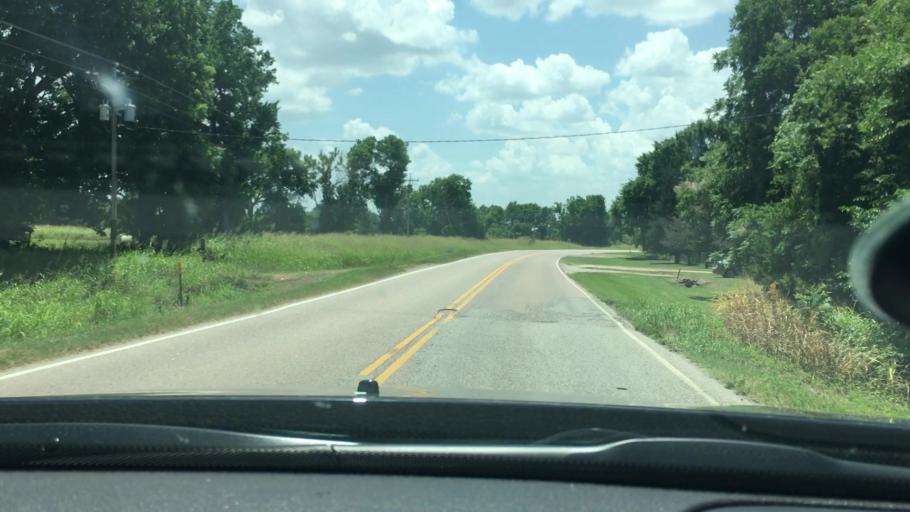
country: US
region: Oklahoma
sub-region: Johnston County
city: Tishomingo
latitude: 34.4861
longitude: -96.6267
